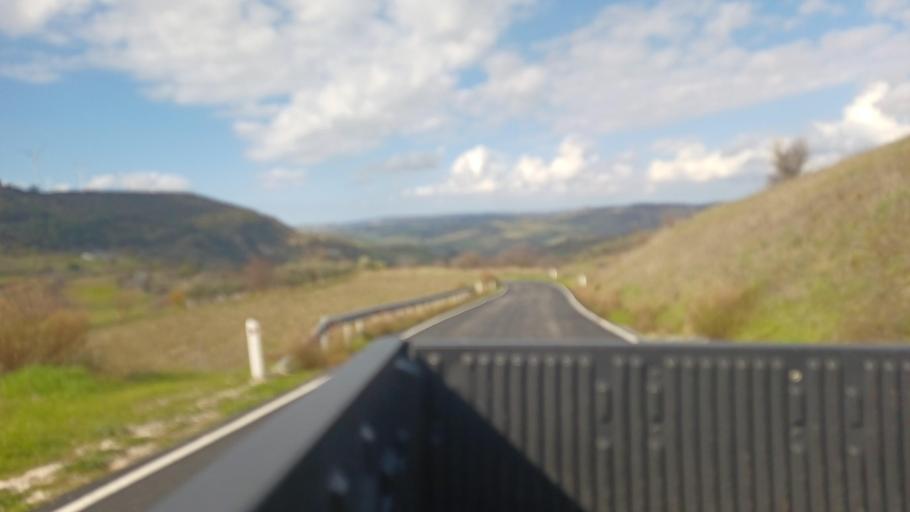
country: CY
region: Limassol
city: Pissouri
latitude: 34.7471
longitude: 32.6723
